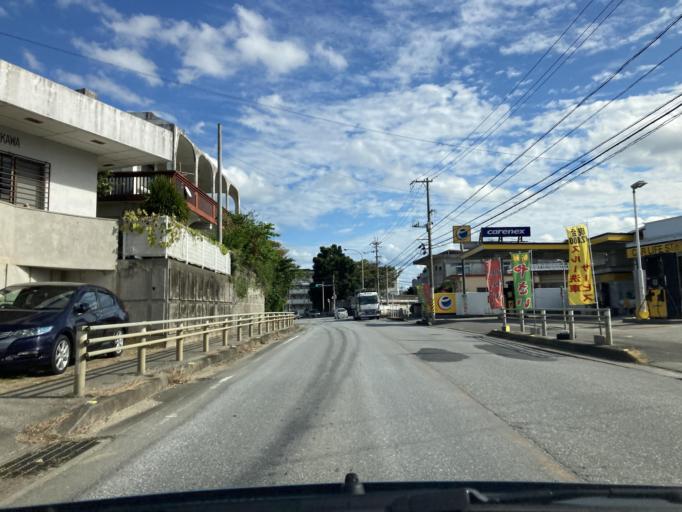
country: JP
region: Okinawa
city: Ishikawa
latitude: 26.4209
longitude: 127.8132
